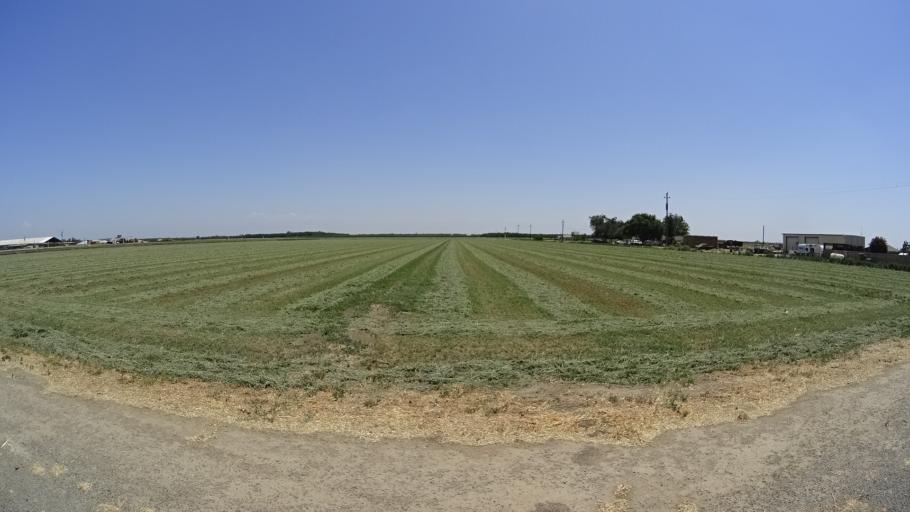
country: US
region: California
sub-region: Kings County
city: Lucerne
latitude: 36.3795
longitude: -119.7270
